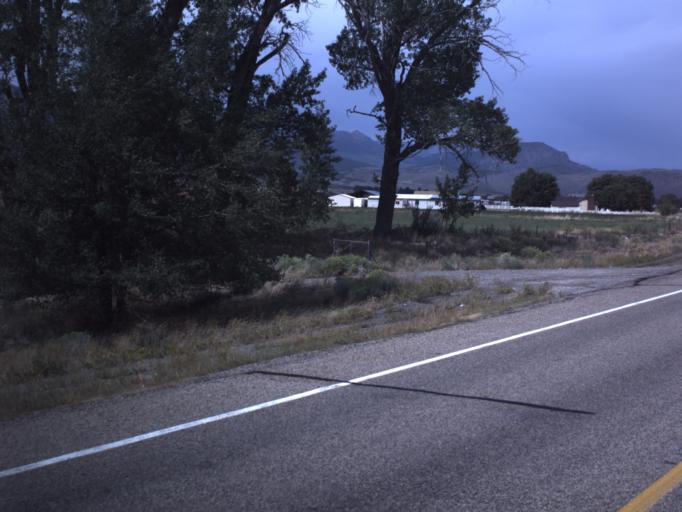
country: US
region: Utah
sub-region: Piute County
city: Junction
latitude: 38.1583
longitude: -112.2802
